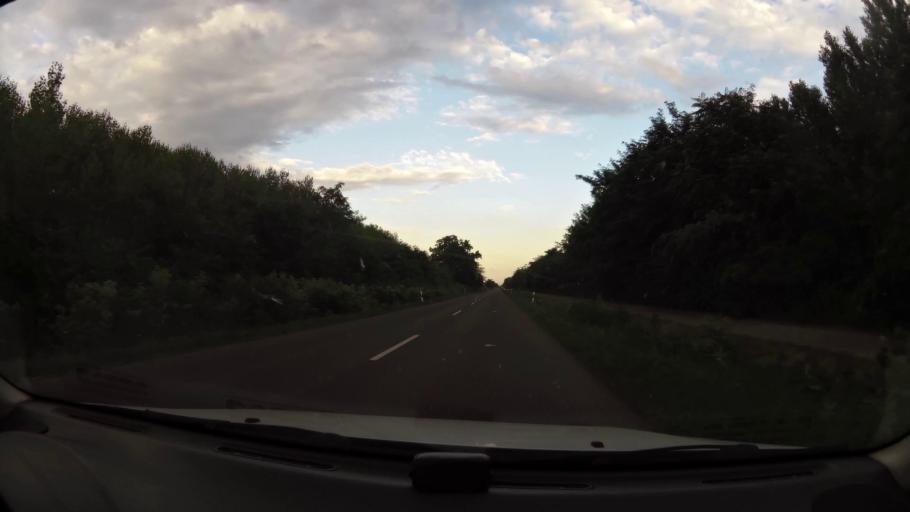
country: HU
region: Pest
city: Ujszilvas
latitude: 47.2843
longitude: 19.9148
